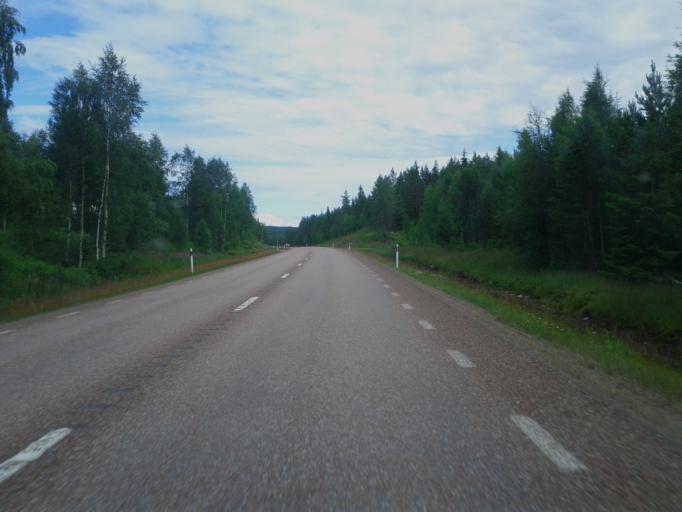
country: SE
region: Dalarna
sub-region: Faluns Kommun
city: Bjursas
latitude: 60.7857
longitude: 15.2925
